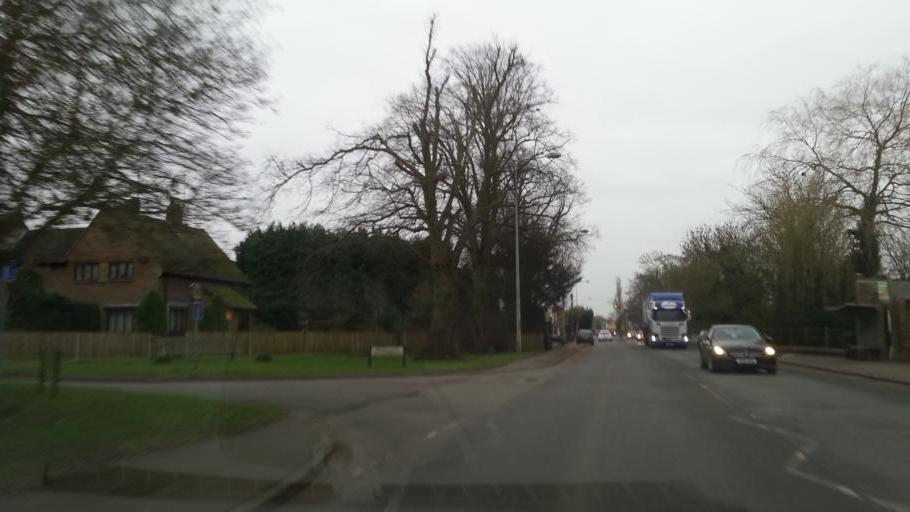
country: GB
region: England
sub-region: Central Bedfordshire
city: Hockliffe
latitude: 51.9290
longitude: -0.5832
